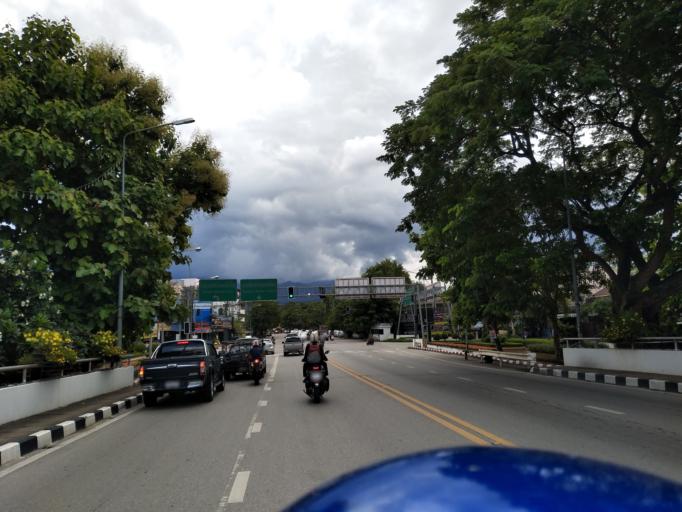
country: TH
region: Chiang Mai
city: Chiang Mai
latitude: 18.7999
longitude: 99.0023
